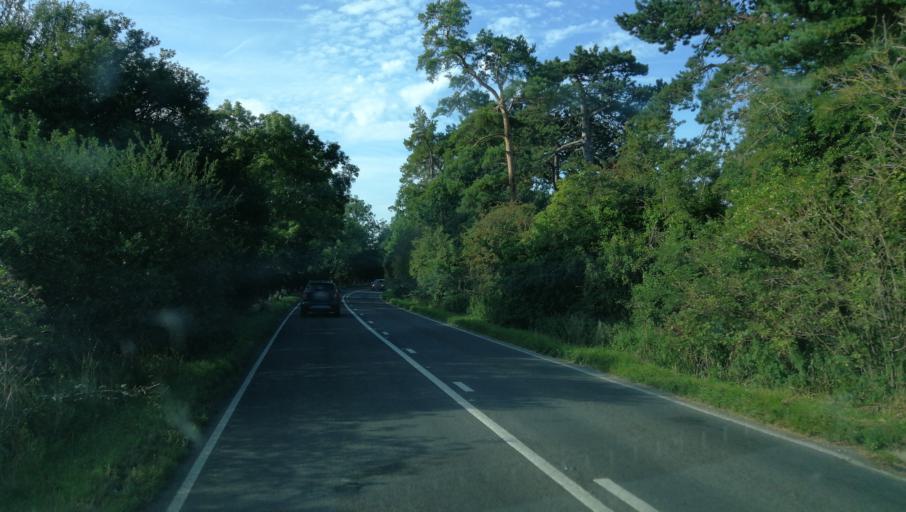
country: GB
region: England
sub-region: Oxfordshire
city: Somerton
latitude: 51.9177
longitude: -1.3251
